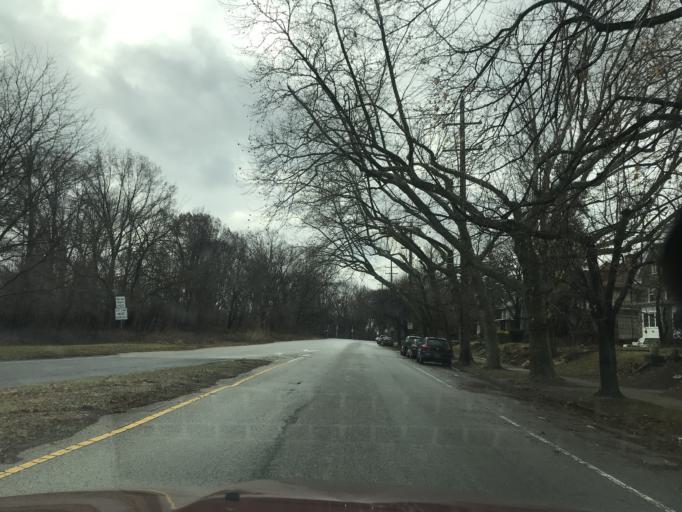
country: US
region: Pennsylvania
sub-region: Montgomery County
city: Bala-Cynwyd
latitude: 39.9919
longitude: -75.2195
